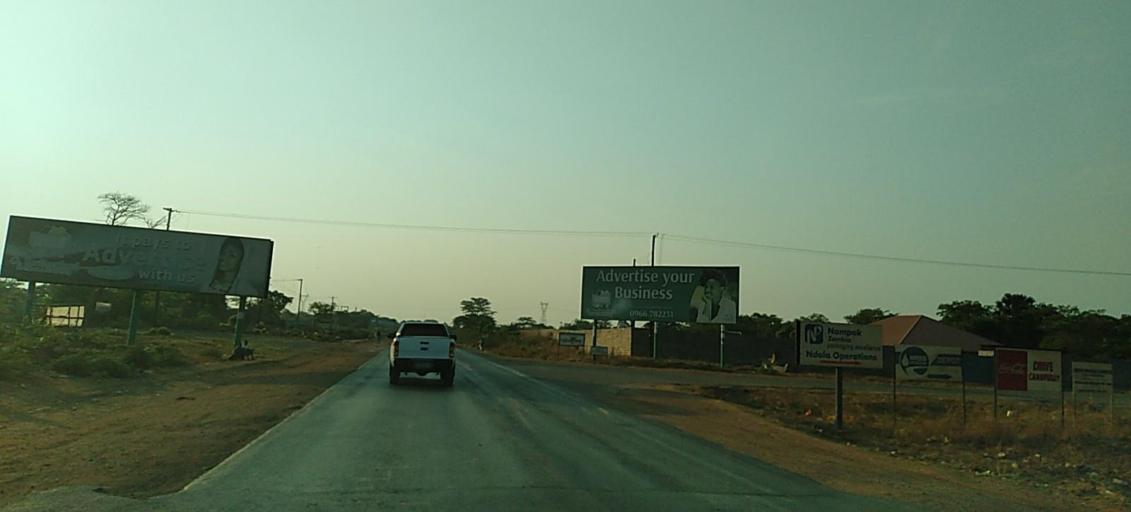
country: ZM
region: Copperbelt
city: Ndola
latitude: -13.0404
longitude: 28.6939
